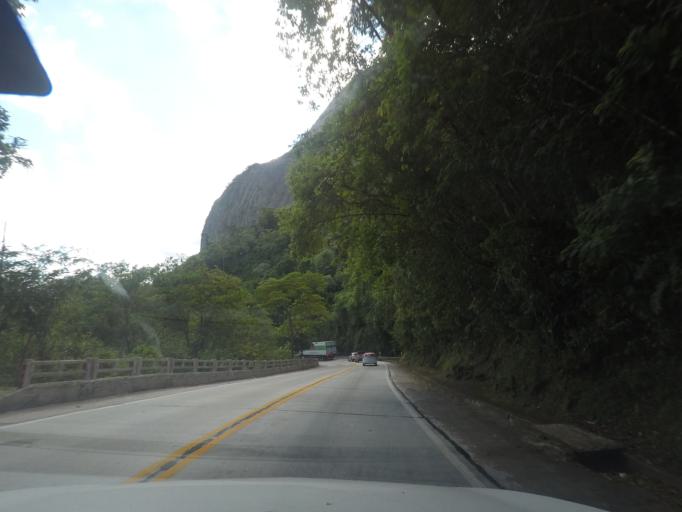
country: BR
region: Rio de Janeiro
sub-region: Guapimirim
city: Guapimirim
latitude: -22.4804
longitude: -42.9979
